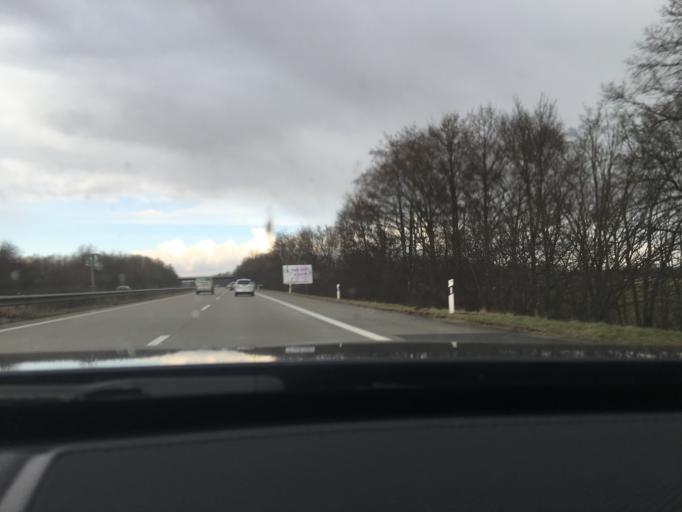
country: DE
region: Lower Saxony
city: Loxstedt
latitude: 53.4807
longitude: 8.6192
